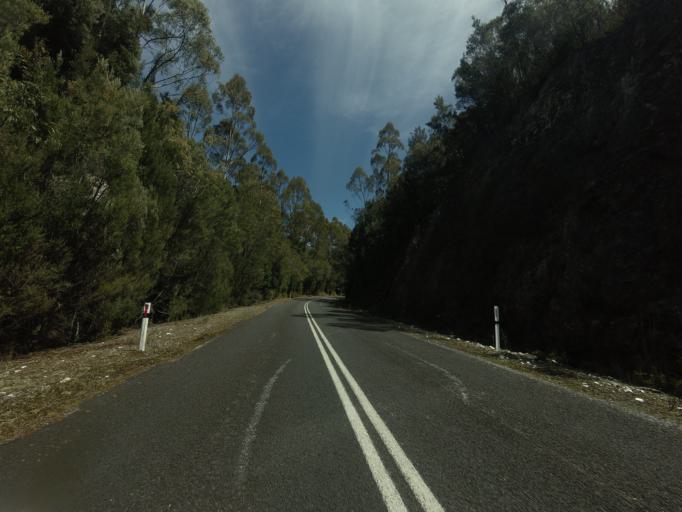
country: AU
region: Tasmania
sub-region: Huon Valley
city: Geeveston
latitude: -42.8209
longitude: 146.1095
